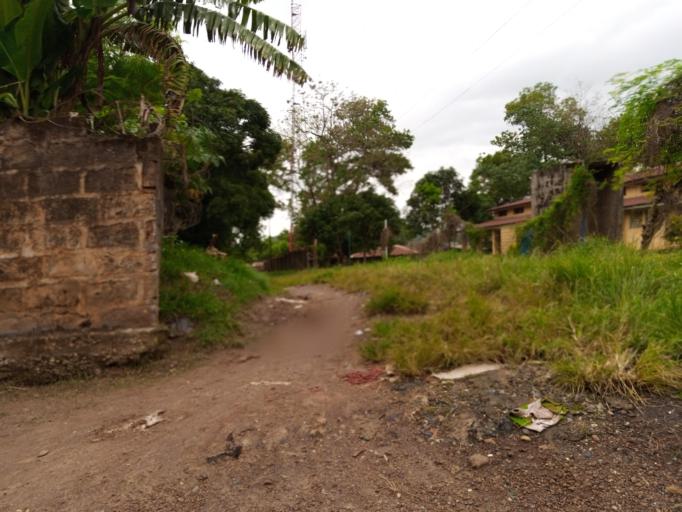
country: SL
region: Eastern Province
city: Kenema
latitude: 7.8620
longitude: -11.1975
